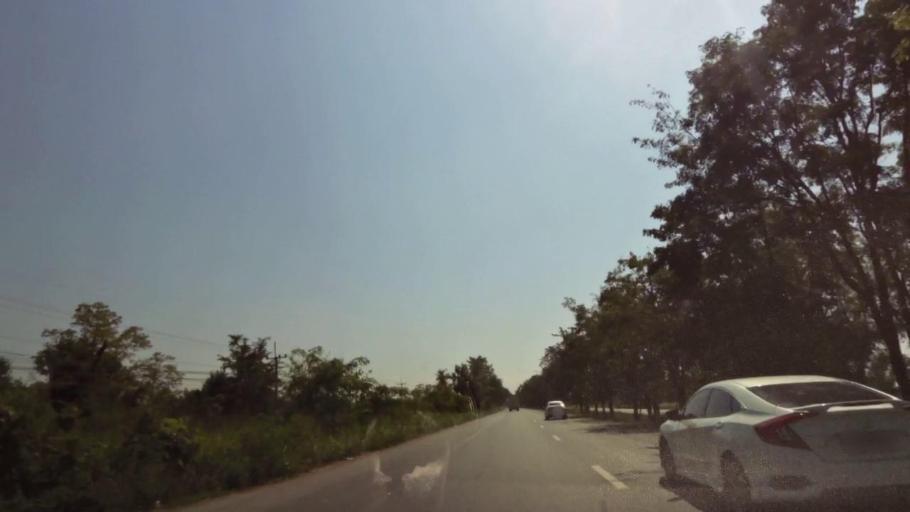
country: TH
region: Nakhon Sawan
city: Kao Liao
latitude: 15.9103
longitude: 100.1123
